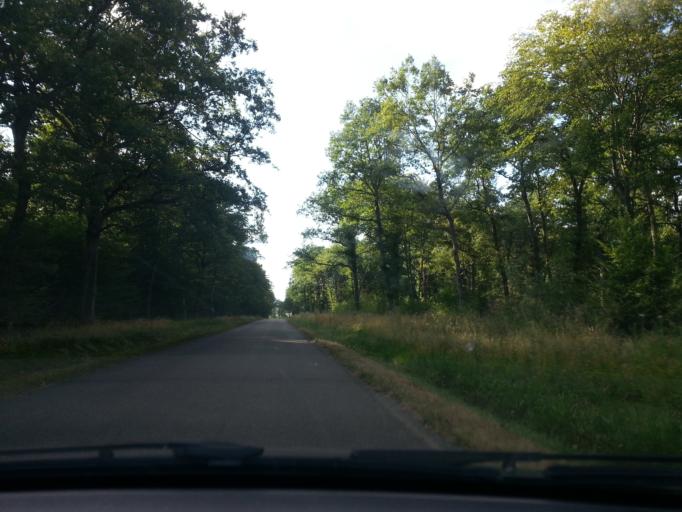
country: FR
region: Bourgogne
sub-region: Departement de Saone-et-Loire
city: Dracy-le-Fort
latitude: 46.7686
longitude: 4.7694
